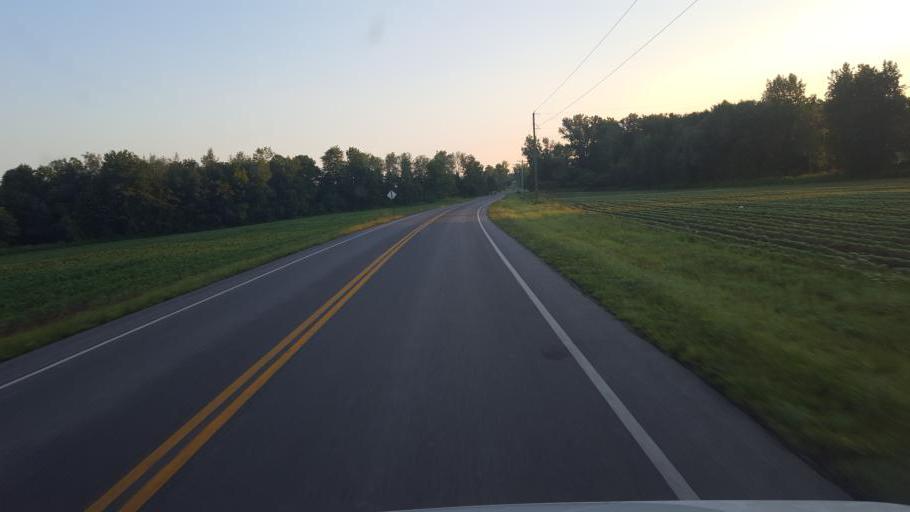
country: US
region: New York
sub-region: Wayne County
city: Clyde
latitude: 43.0736
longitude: -76.8915
